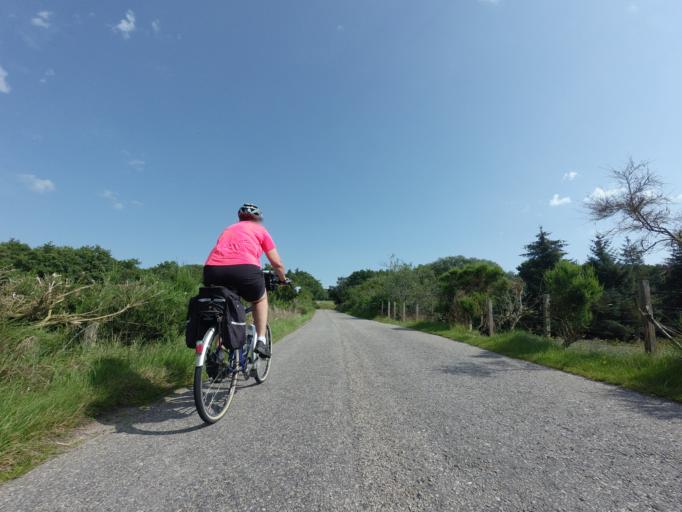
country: GB
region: Scotland
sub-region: Highland
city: Invergordon
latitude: 57.7535
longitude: -4.1581
